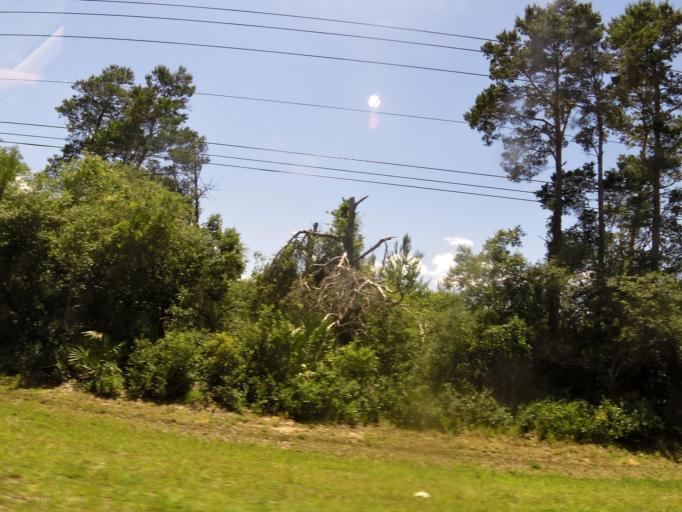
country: US
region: Florida
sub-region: Flagler County
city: Flagler Beach
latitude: 29.4430
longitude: -81.1610
